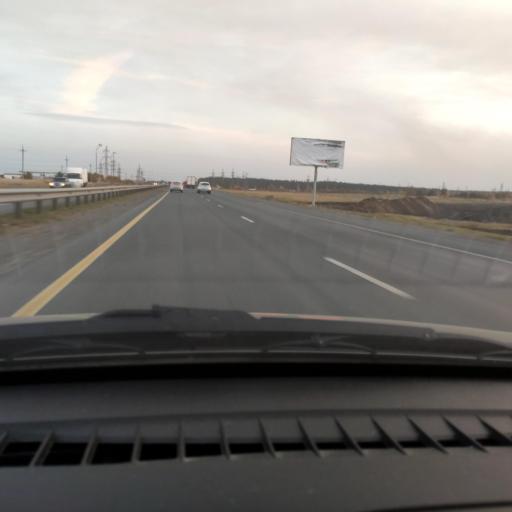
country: RU
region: Samara
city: Zhigulevsk
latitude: 53.5494
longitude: 49.5082
